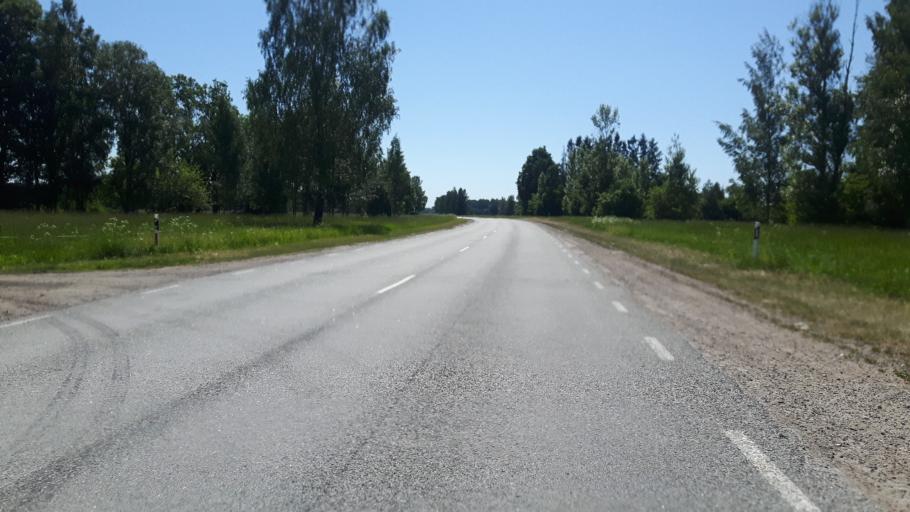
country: EE
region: Paernumaa
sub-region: Tootsi vald
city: Tootsi
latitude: 58.4631
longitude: 24.7830
